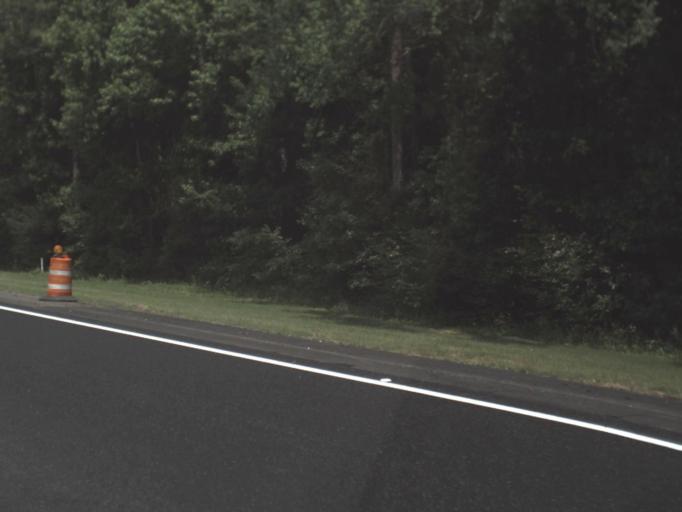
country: US
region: Florida
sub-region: Nassau County
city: Nassau Village-Ratliff
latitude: 30.4427
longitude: -81.7215
